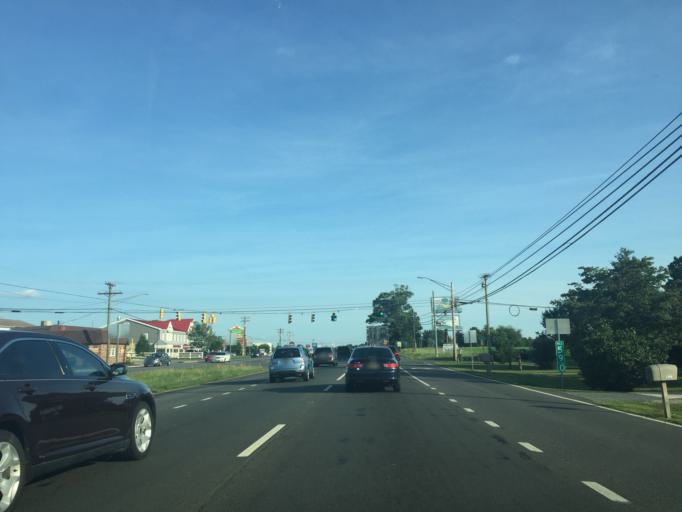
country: US
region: Delaware
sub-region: Kent County
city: Smyrna
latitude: 39.2704
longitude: -75.5892
